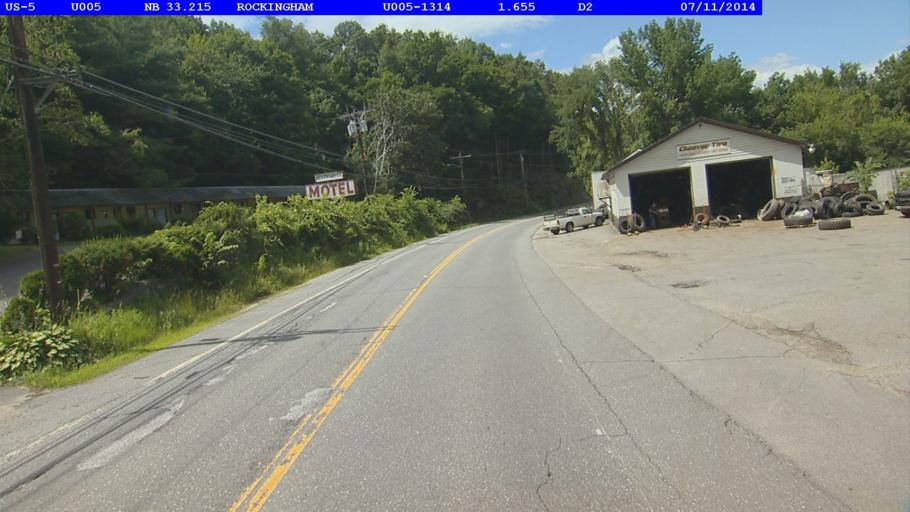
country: US
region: Vermont
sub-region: Windham County
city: Bellows Falls
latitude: 43.1453
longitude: -72.4579
